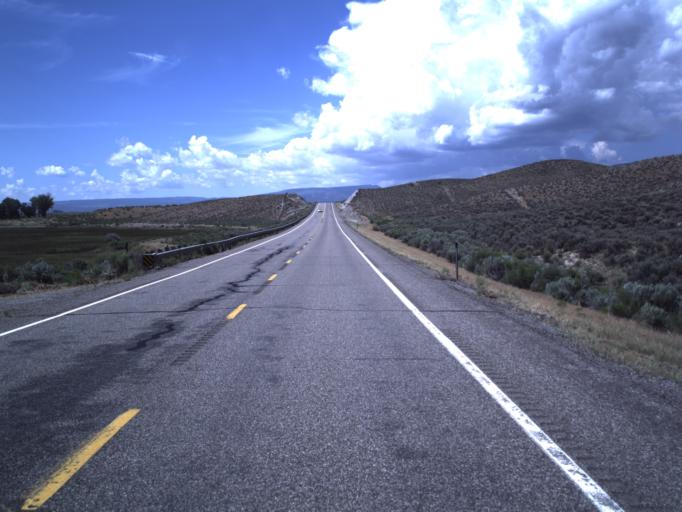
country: US
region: Utah
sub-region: Garfield County
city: Panguitch
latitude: 38.0144
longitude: -112.3714
